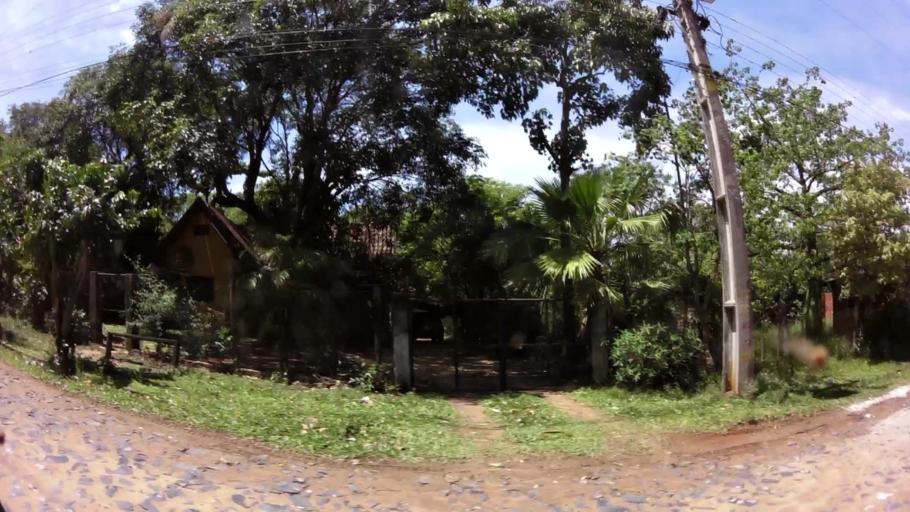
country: PY
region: Central
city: Colonia Mariano Roque Alonso
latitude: -25.2009
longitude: -57.5512
